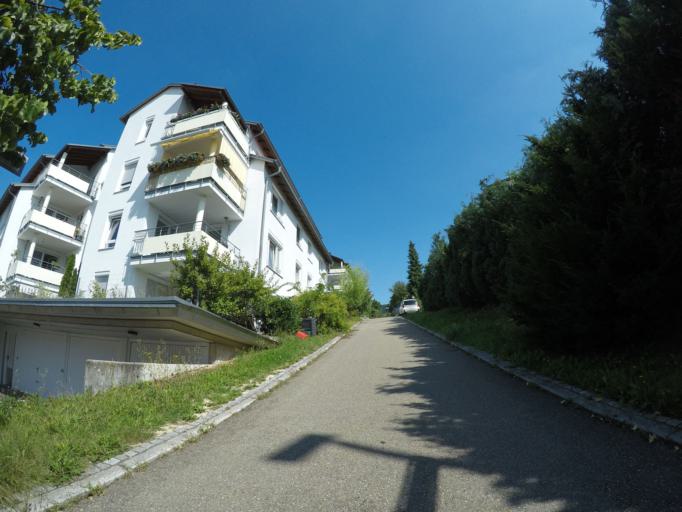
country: DE
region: Baden-Wuerttemberg
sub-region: Tuebingen Region
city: Eningen unter Achalm
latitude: 48.4820
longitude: 9.2567
